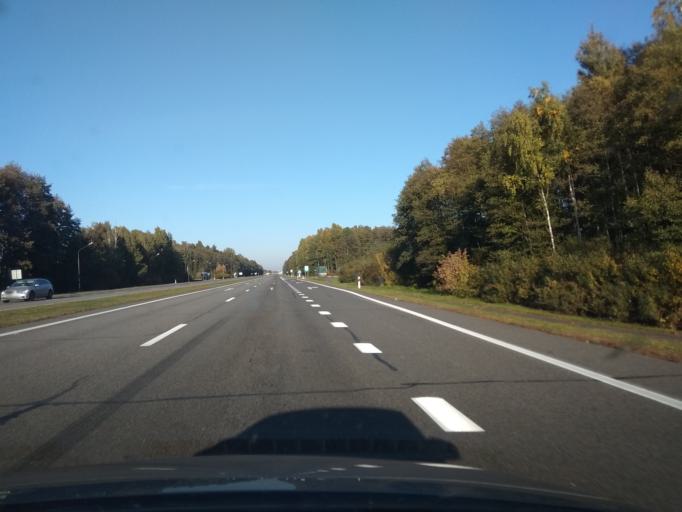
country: BY
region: Brest
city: Ivatsevichy
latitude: 52.6845
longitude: 25.3354
